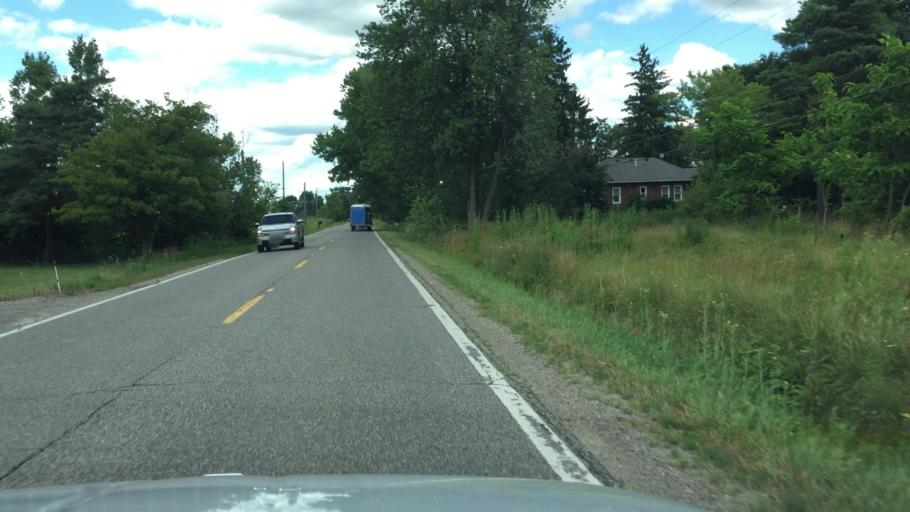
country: US
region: Michigan
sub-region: Macomb County
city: Armada
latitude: 42.8784
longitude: -82.9454
